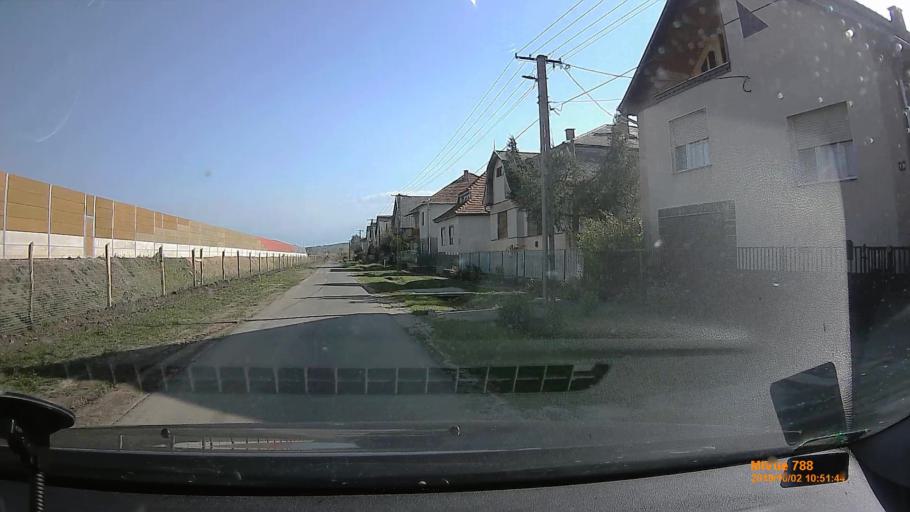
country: HU
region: Nograd
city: Matraverebely
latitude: 47.9744
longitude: 19.7815
